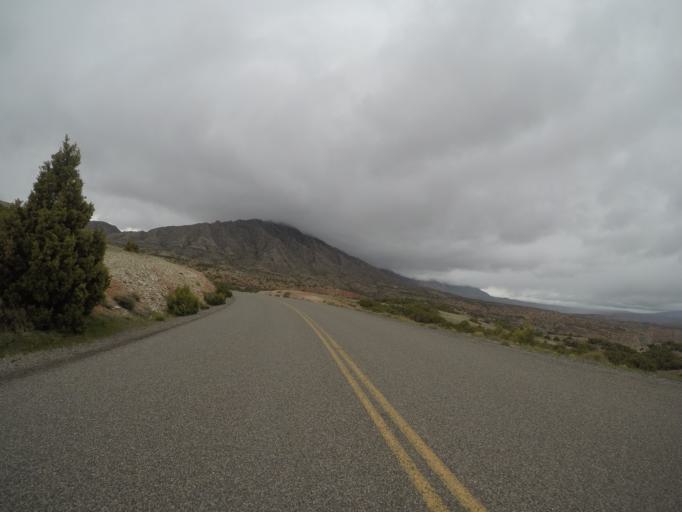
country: US
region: Wyoming
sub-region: Big Horn County
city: Lovell
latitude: 45.0243
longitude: -108.2556
